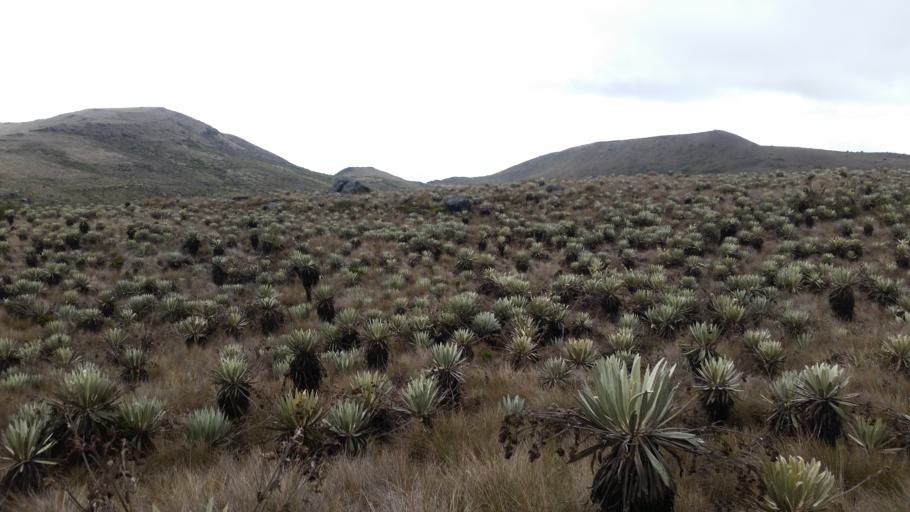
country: CO
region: Cundinamarca
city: Pasca
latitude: 4.3696
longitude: -74.2173
